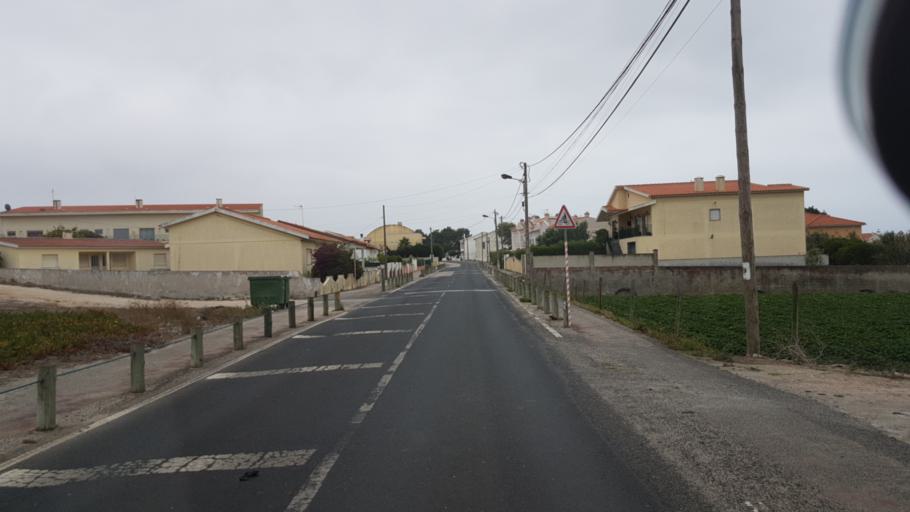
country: PT
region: Lisbon
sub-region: Torres Vedras
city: Silveira
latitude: 39.1490
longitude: -9.3632
